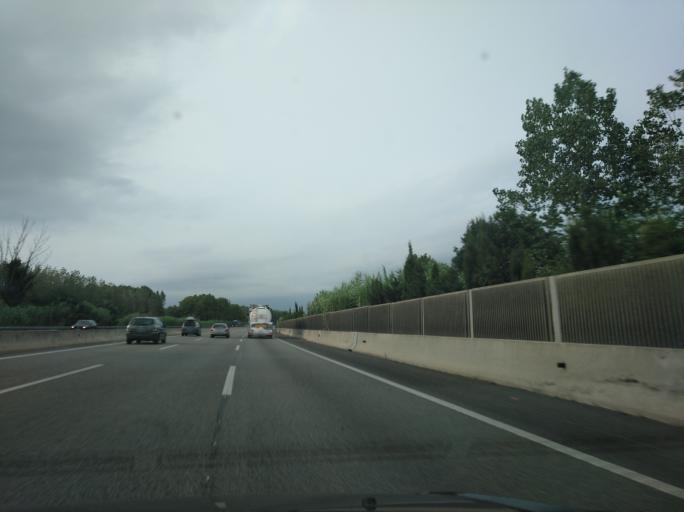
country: ES
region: Catalonia
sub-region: Provincia de Girona
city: Sils
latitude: 41.8191
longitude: 2.7460
